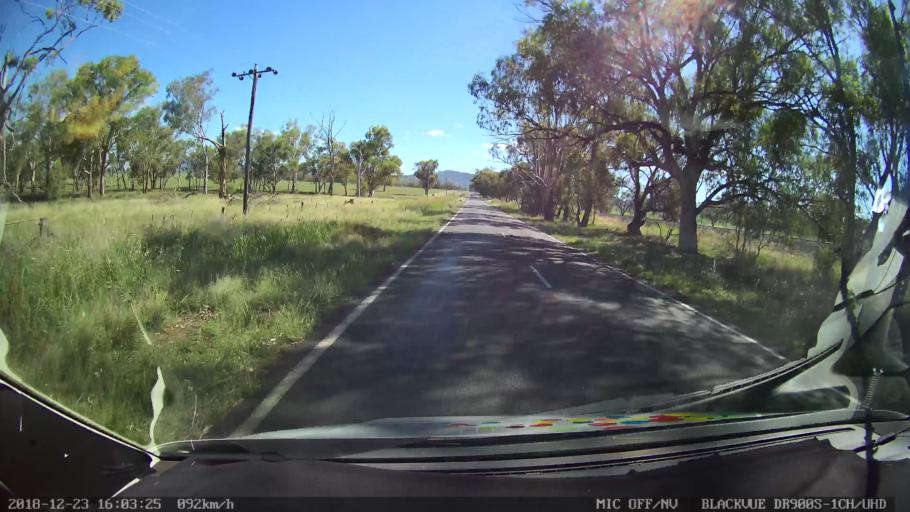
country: AU
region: New South Wales
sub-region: Tamworth Municipality
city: Phillip
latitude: -31.2433
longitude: 150.8010
